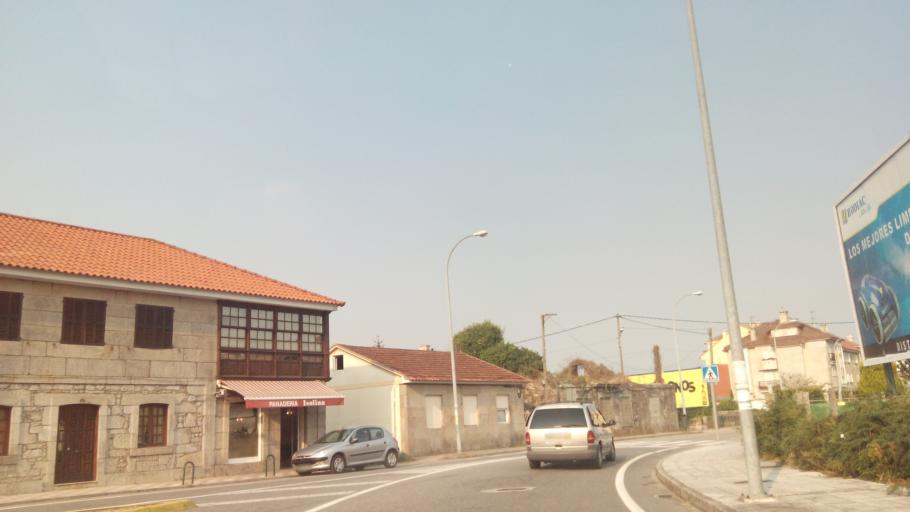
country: ES
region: Galicia
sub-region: Provincia de Pontevedra
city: Baiona
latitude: 42.1101
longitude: -8.8256
